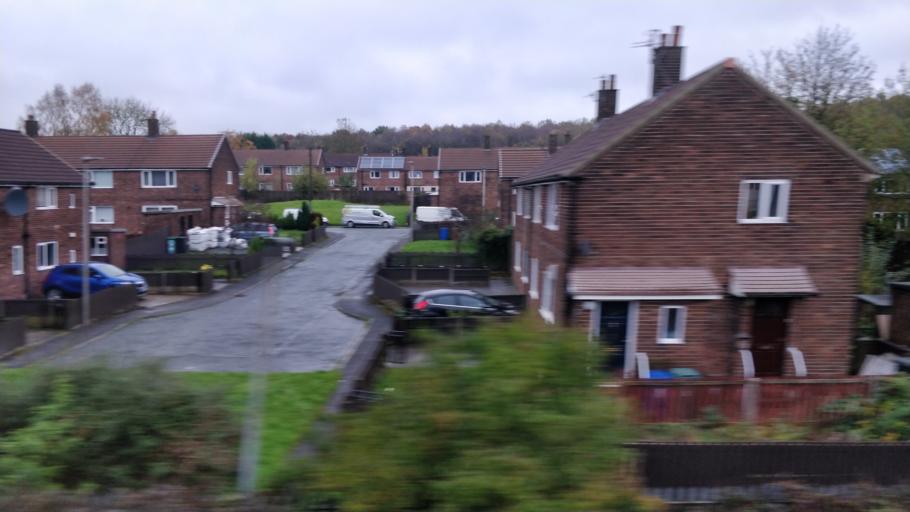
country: GB
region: England
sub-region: Borough of Wigan
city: Atherton
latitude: 53.5331
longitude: -2.4919
